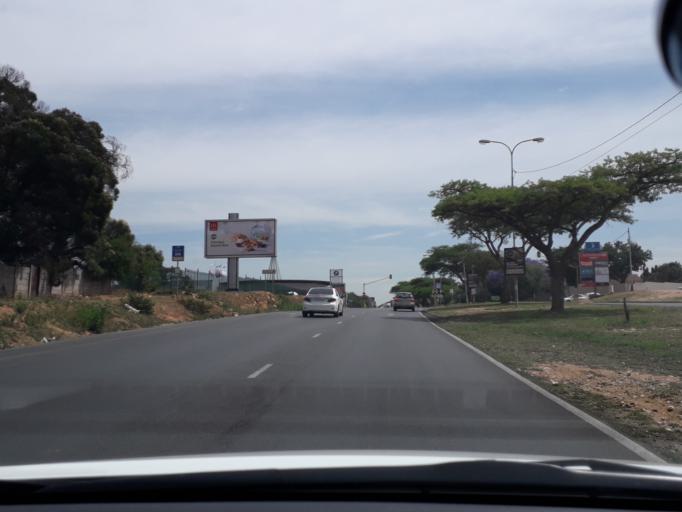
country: ZA
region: Gauteng
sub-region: City of Johannesburg Metropolitan Municipality
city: Midrand
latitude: -26.0649
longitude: 28.0246
